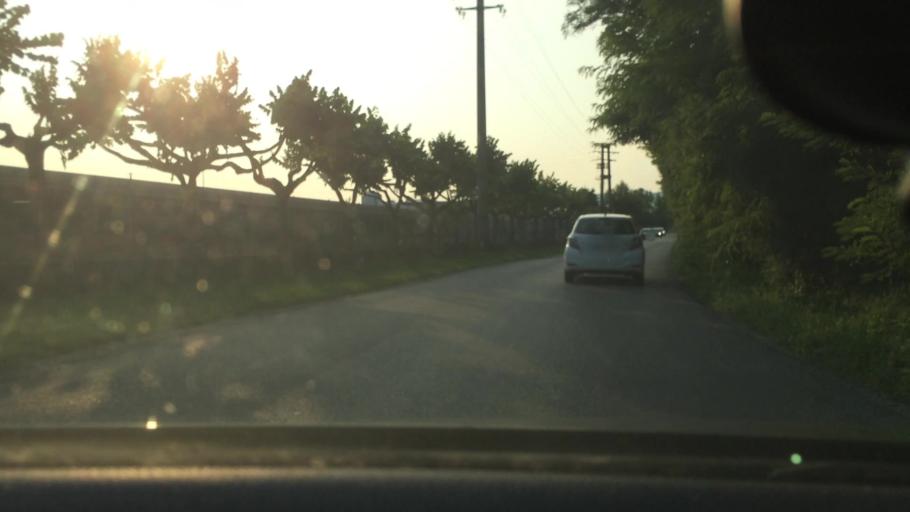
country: IT
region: Lombardy
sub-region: Provincia di Bergamo
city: Brembate di Sopra
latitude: 45.7100
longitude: 9.5724
